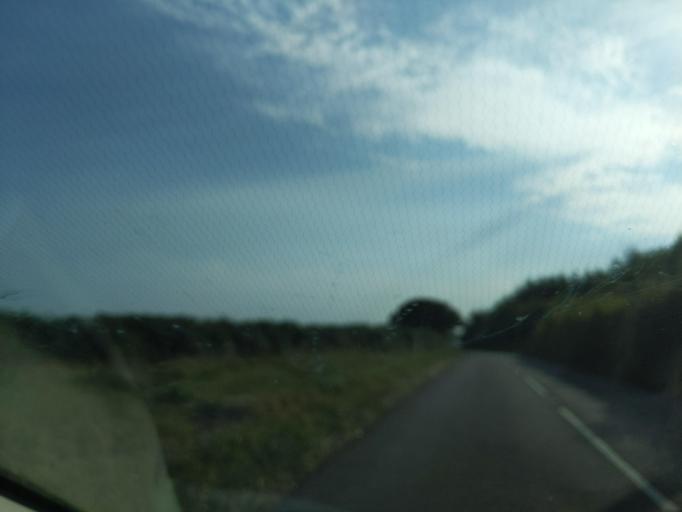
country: GB
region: England
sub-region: Devon
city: Great Torrington
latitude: 50.9745
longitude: -4.0646
